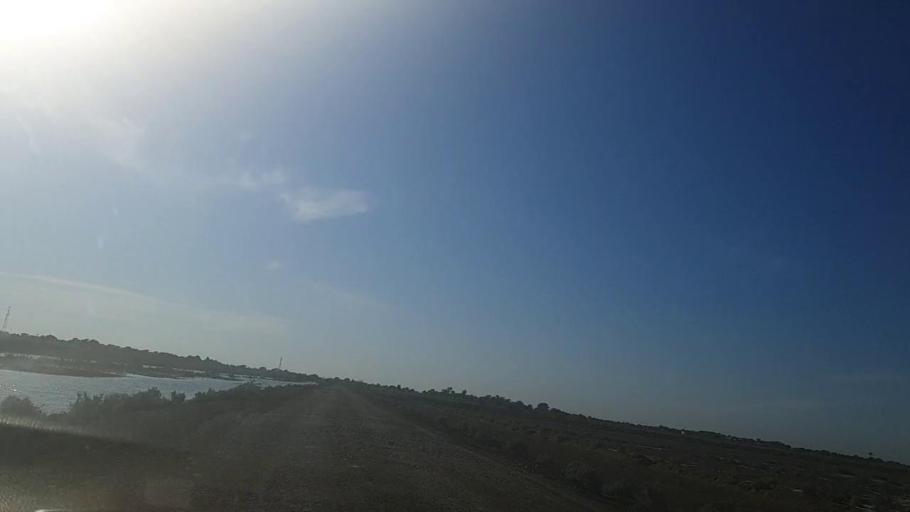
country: PK
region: Sindh
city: Pithoro
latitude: 25.5110
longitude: 69.4004
